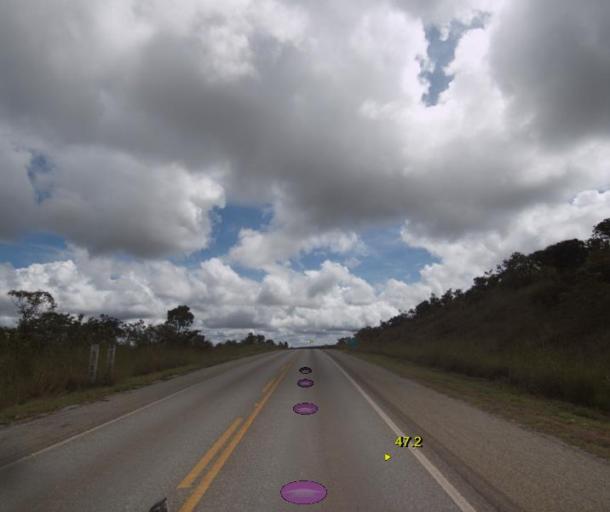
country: BR
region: Goias
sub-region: Pirenopolis
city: Pirenopolis
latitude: -15.7523
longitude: -48.5915
